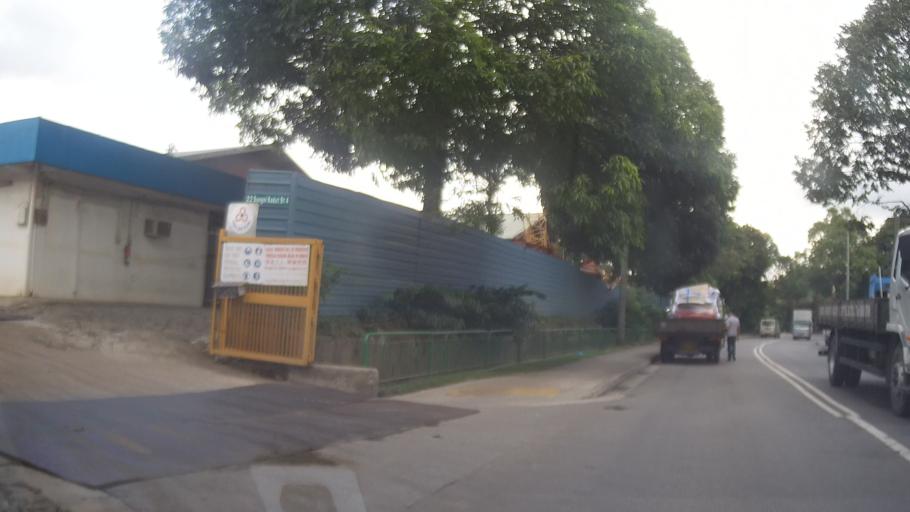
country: MY
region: Johor
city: Johor Bahru
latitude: 1.4211
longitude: 103.7475
